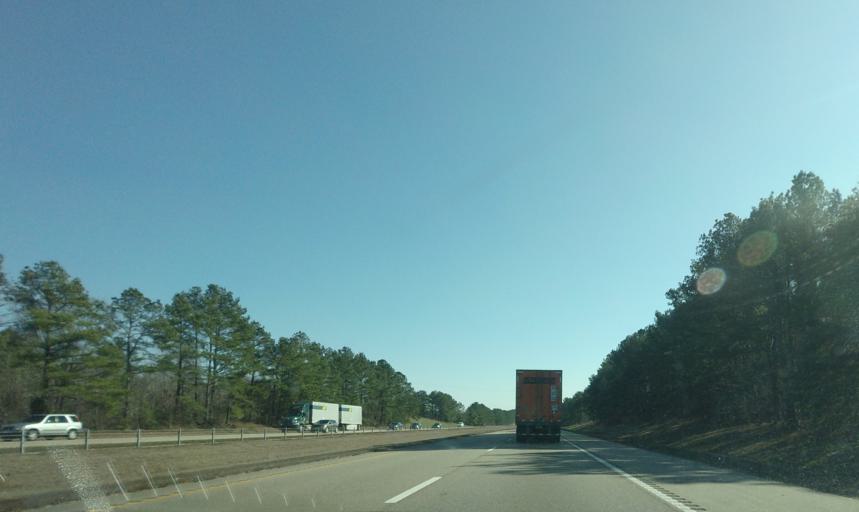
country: US
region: Mississippi
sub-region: Marshall County
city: Holly Springs
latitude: 34.7345
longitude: -89.4353
